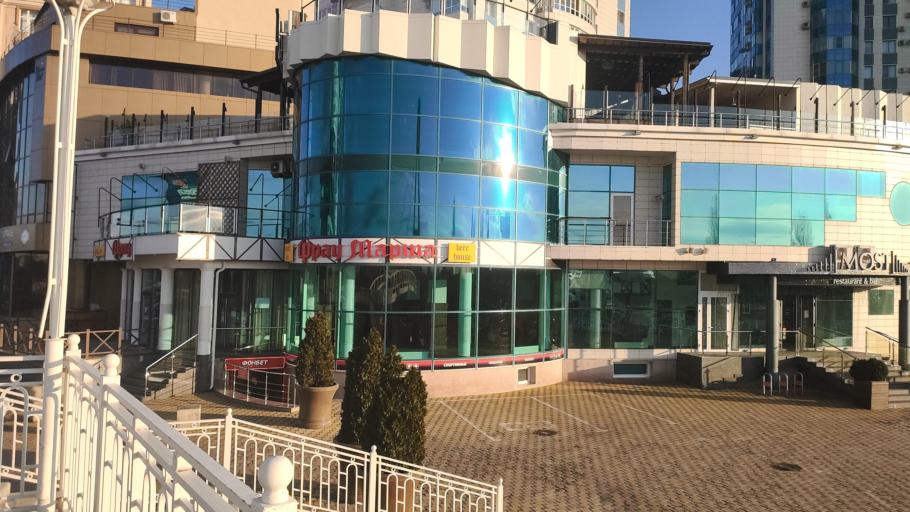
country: RU
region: Krasnodarskiy
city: Krasnodar
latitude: 45.0251
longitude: 38.9582
